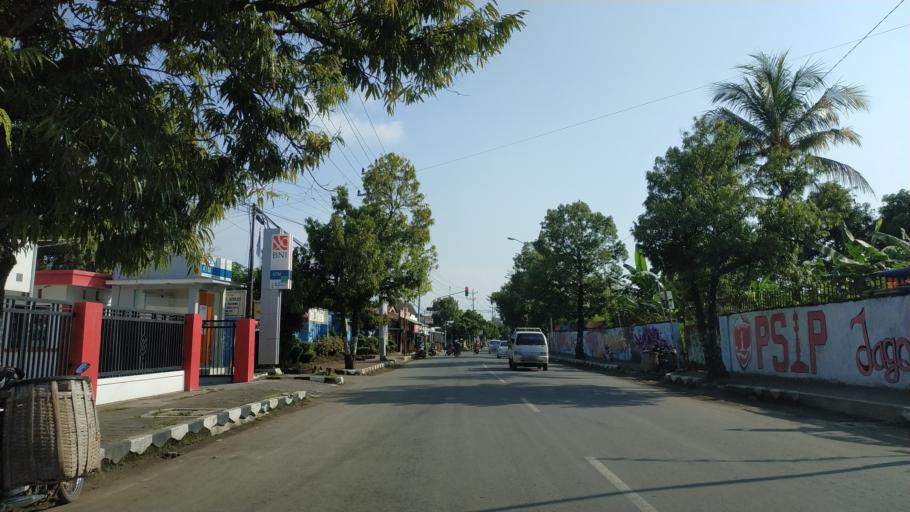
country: ID
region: Central Java
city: Pemalang
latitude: -6.9009
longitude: 109.3878
